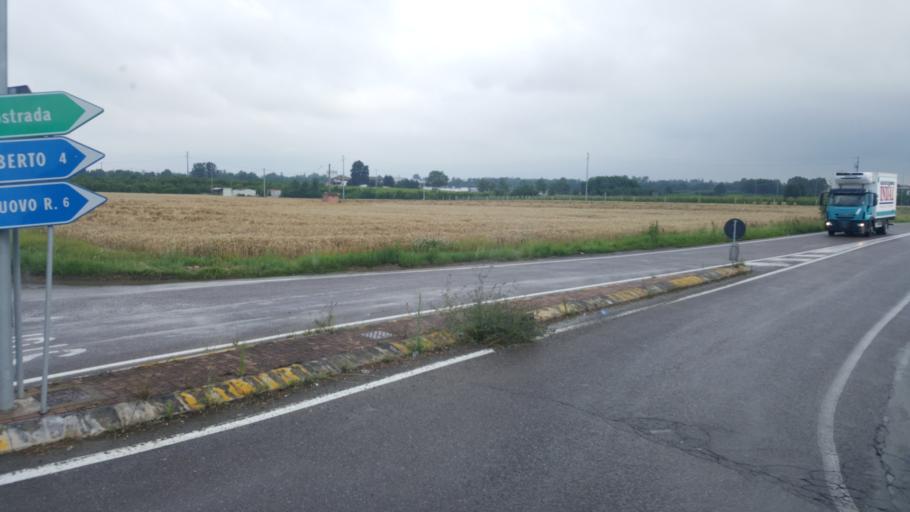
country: IT
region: Emilia-Romagna
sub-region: Provincia di Modena
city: Spilamberto
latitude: 44.5187
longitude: 10.9866
